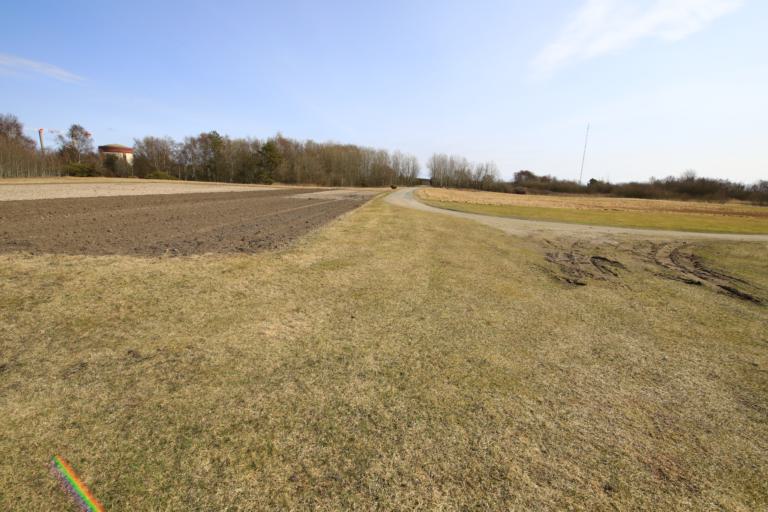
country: SE
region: Halland
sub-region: Kungsbacka Kommun
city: Frillesas
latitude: 57.2540
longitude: 12.1000
